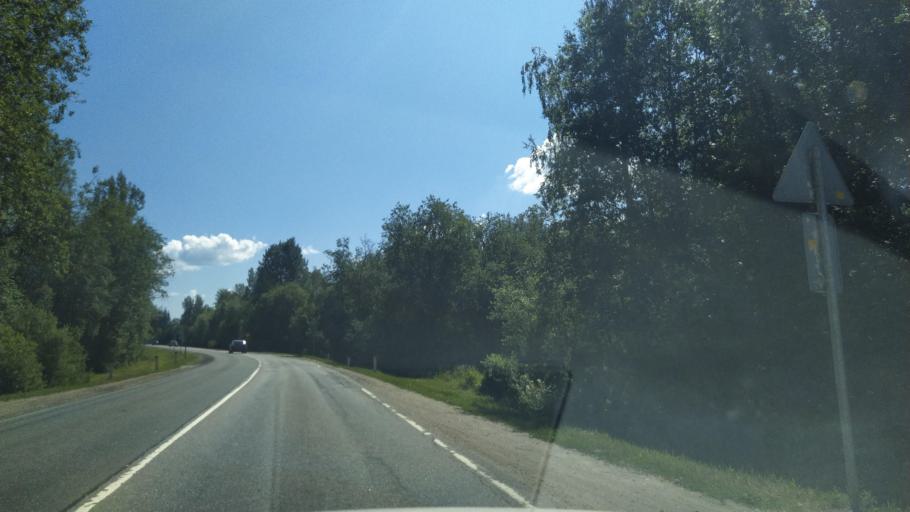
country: RU
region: Leningrad
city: Kirovsk
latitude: 59.9262
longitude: 30.9651
